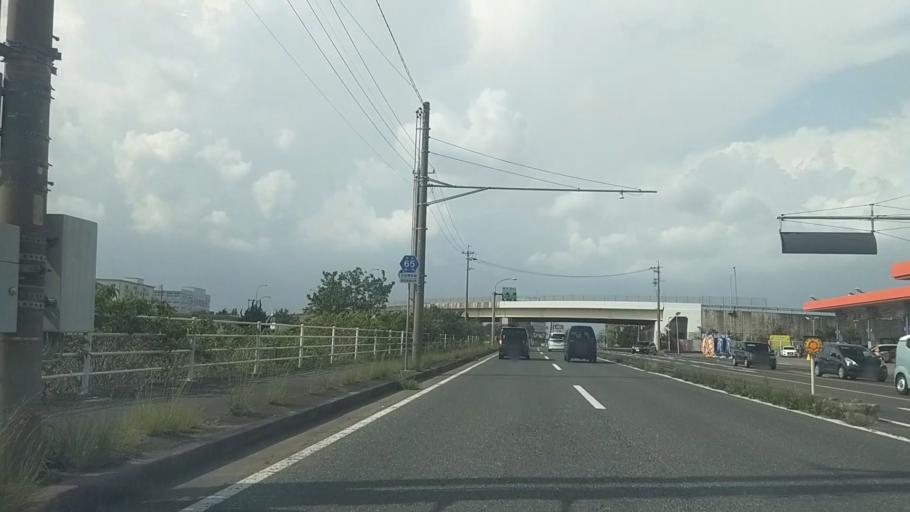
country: JP
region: Shizuoka
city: Hamakita
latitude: 34.7417
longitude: 137.7901
